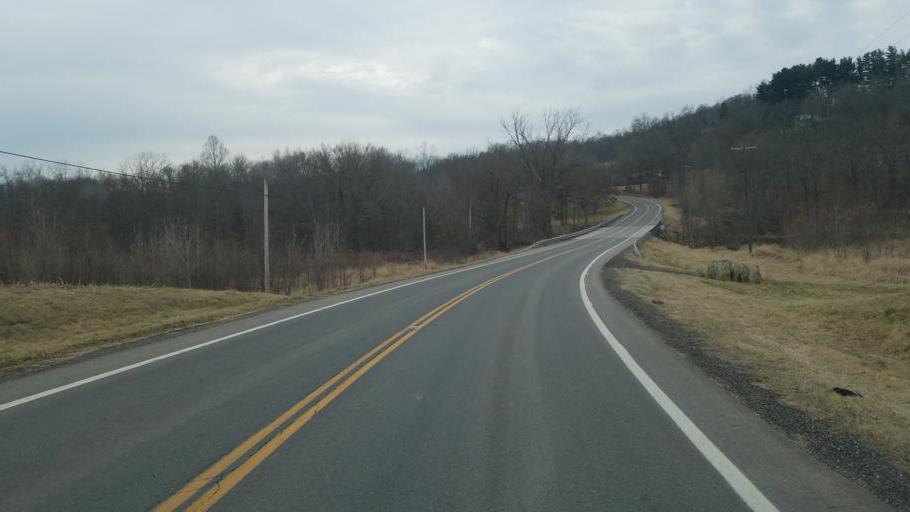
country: US
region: Ohio
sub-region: Richland County
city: Lincoln Heights
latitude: 40.7216
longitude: -82.3722
